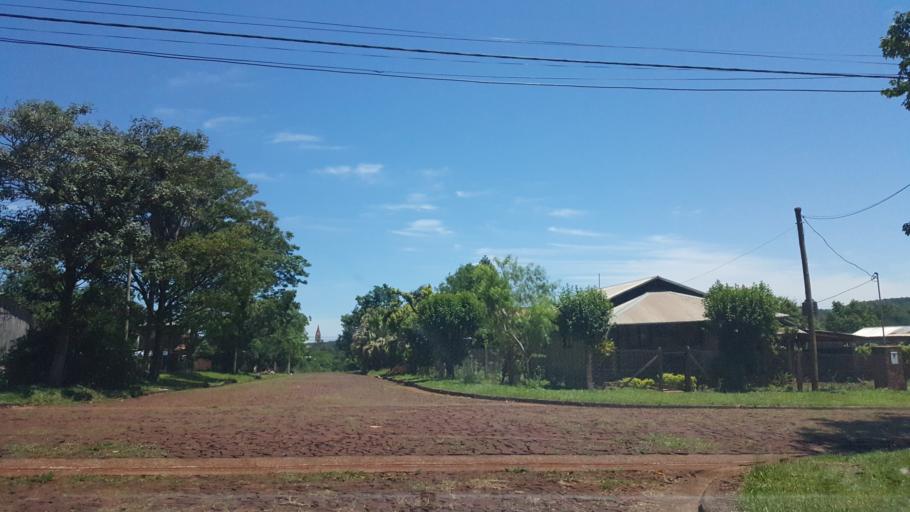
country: AR
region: Misiones
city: Capiovi
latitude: -26.9276
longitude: -55.0503
